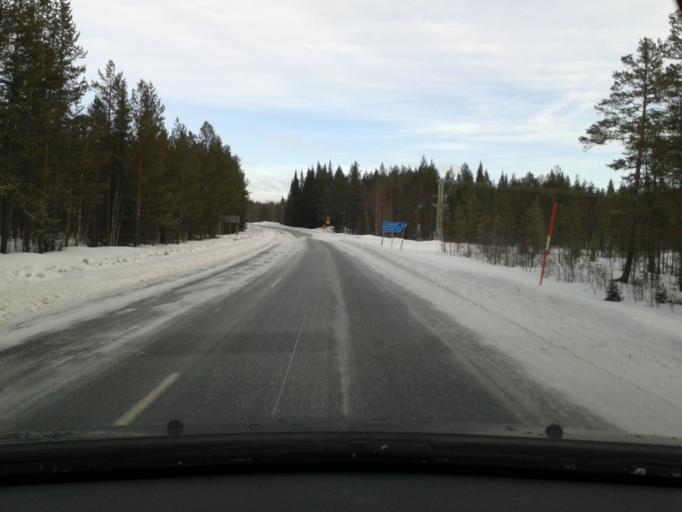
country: SE
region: Vaesterbotten
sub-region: Vilhelmina Kommun
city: Vilhelmina
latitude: 64.6448
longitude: 16.5015
